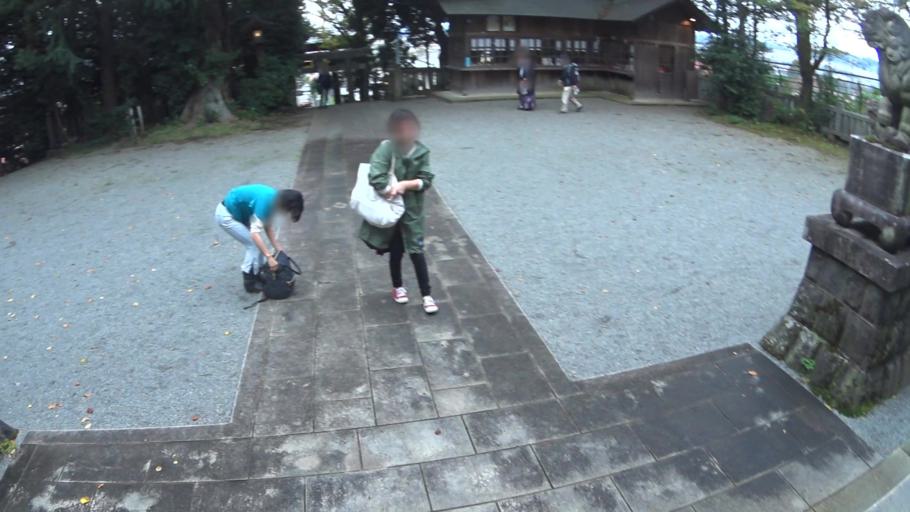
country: JP
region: Kanagawa
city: Hadano
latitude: 35.3796
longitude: 139.2206
